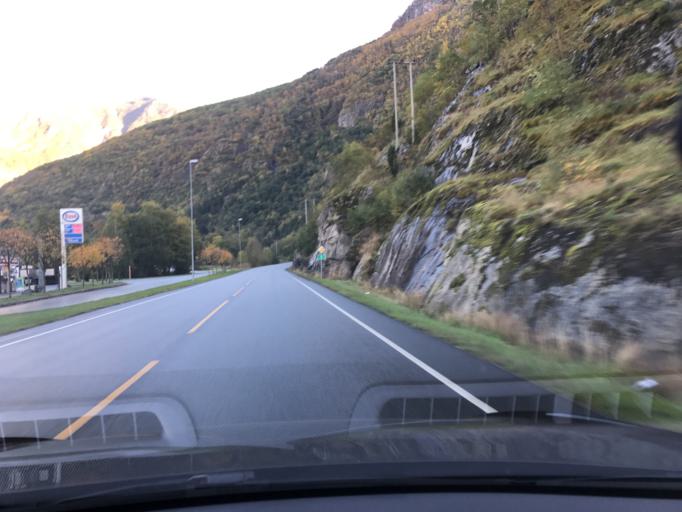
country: NO
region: Sogn og Fjordane
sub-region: Laerdal
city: Laerdalsoyri
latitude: 61.0977
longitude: 7.4735
